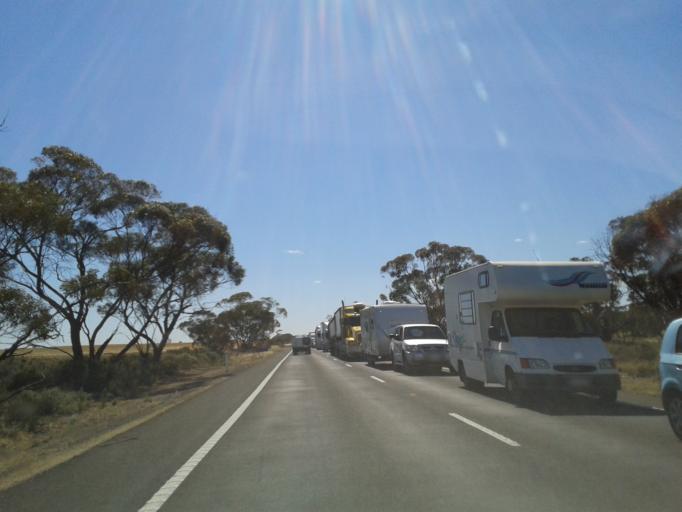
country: AU
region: New South Wales
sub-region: Wentworth
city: Dareton
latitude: -34.2699
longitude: 141.8009
